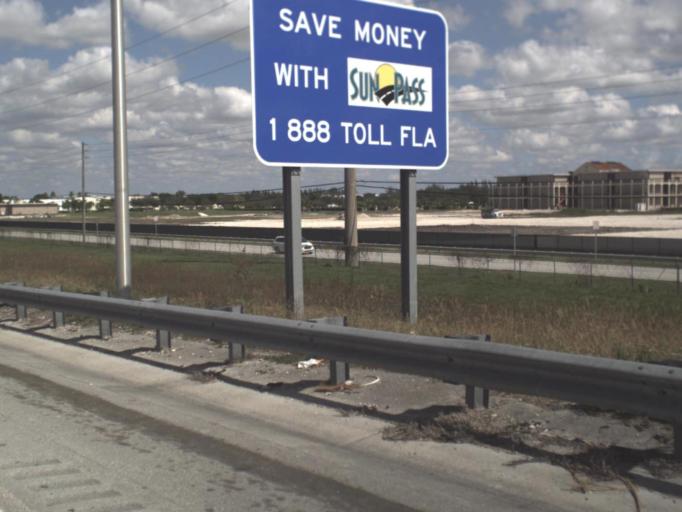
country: US
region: Florida
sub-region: Miami-Dade County
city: Doral
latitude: 25.7991
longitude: -80.3858
